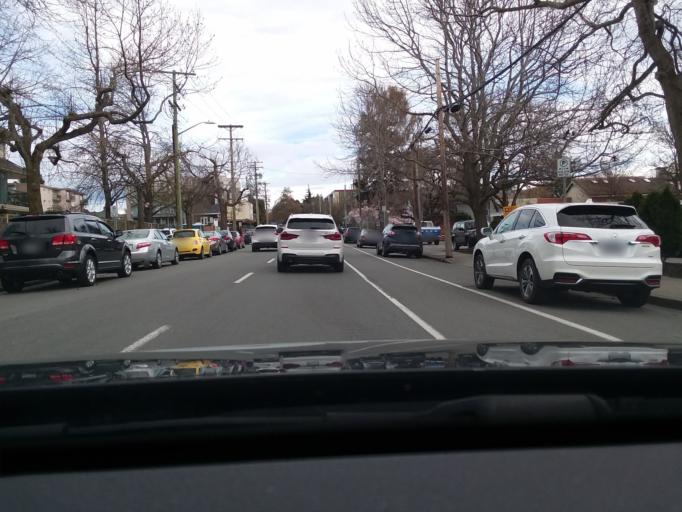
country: CA
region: British Columbia
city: Victoria
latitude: 48.4258
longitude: -123.3523
